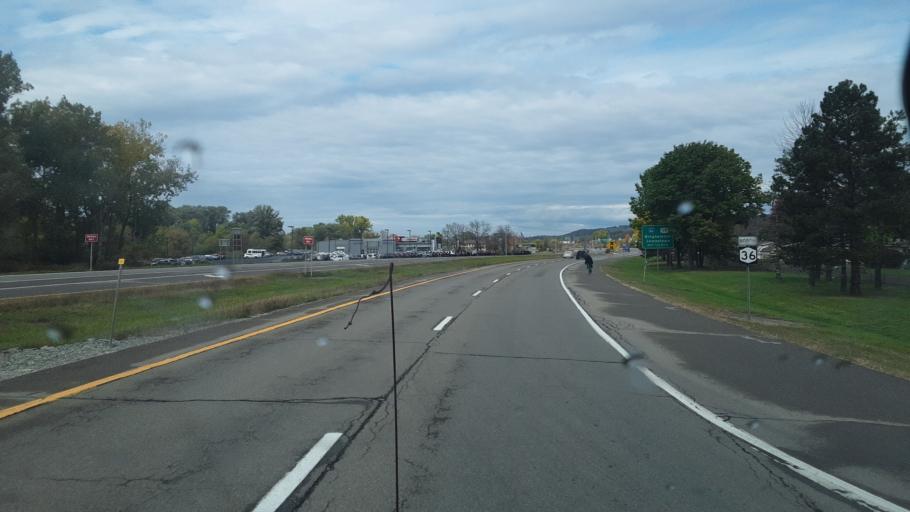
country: US
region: New York
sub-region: Steuben County
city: Hornell
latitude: 42.3628
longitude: -77.6728
